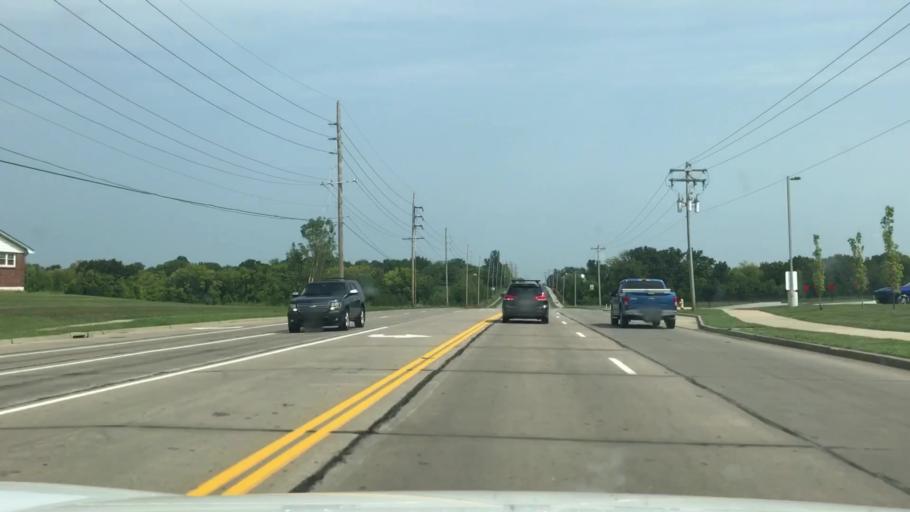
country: US
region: Missouri
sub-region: Saint Charles County
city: Dardenne Prairie
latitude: 38.7736
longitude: -90.7375
